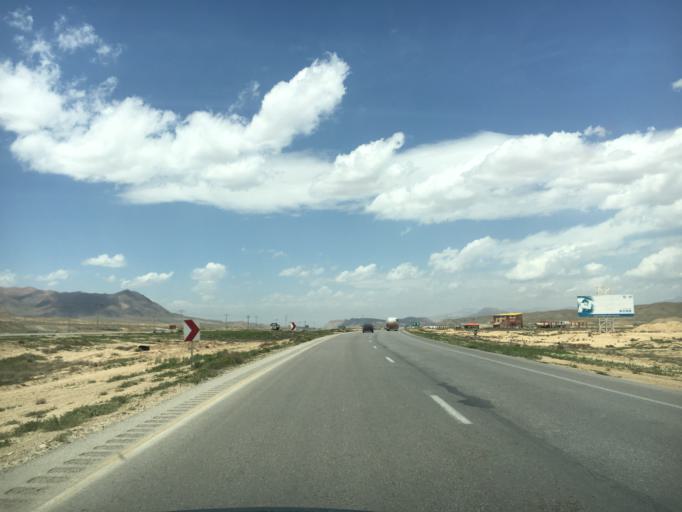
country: IR
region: Markazi
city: Delijan
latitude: 33.7640
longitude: 50.8538
